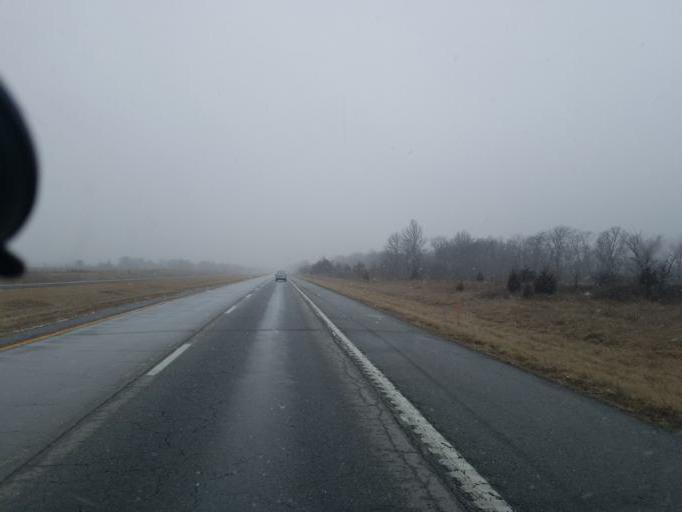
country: US
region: Missouri
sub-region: Macon County
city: La Plata
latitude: 39.9786
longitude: -92.4761
